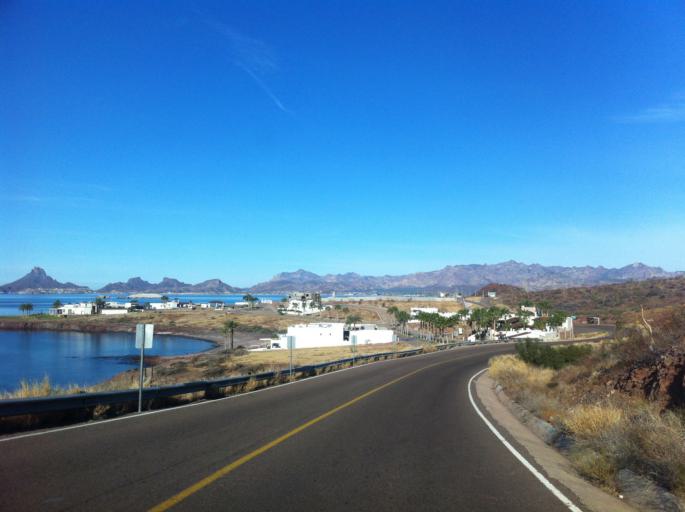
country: MX
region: Sonora
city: Heroica Guaymas
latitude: 27.9278
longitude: -110.9617
